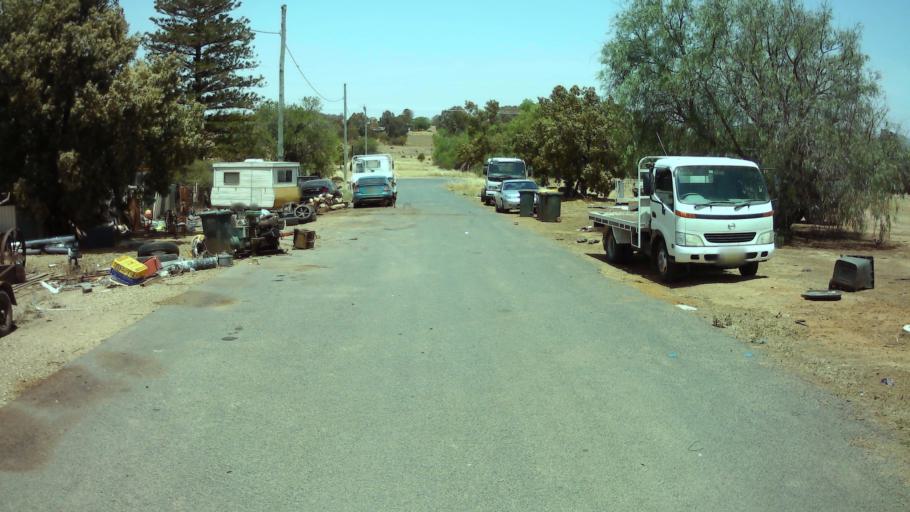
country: AU
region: New South Wales
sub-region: Weddin
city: Grenfell
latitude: -33.8971
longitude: 148.1709
